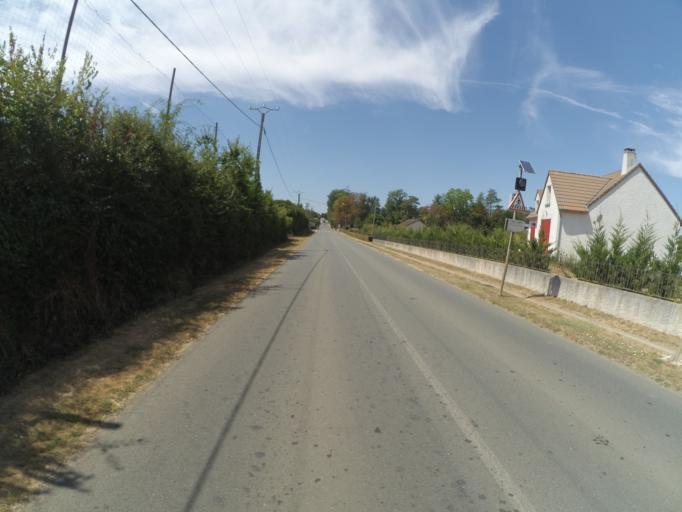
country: FR
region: Poitou-Charentes
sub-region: Departement de la Vienne
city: Saint-Maurice-la-Clouere
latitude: 46.3710
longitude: 0.4140
